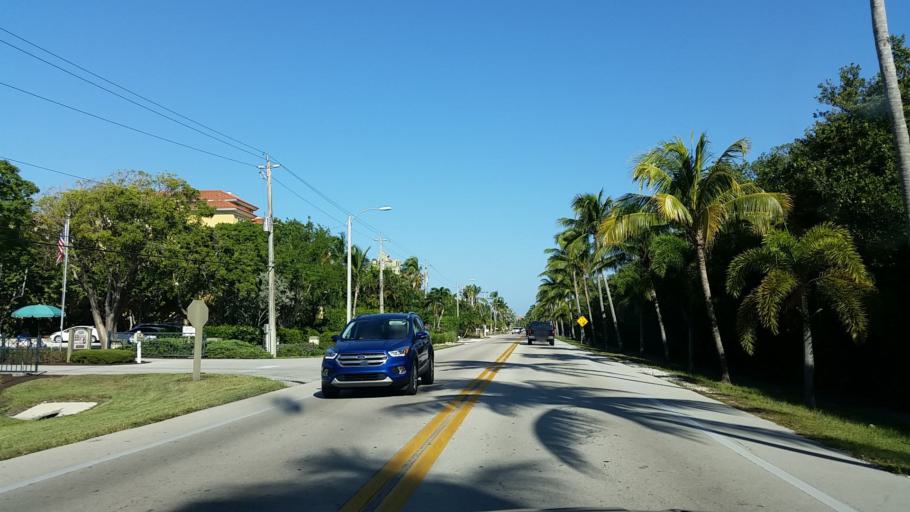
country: US
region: Florida
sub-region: Lee County
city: Bonita Springs
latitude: 26.3419
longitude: -81.8498
